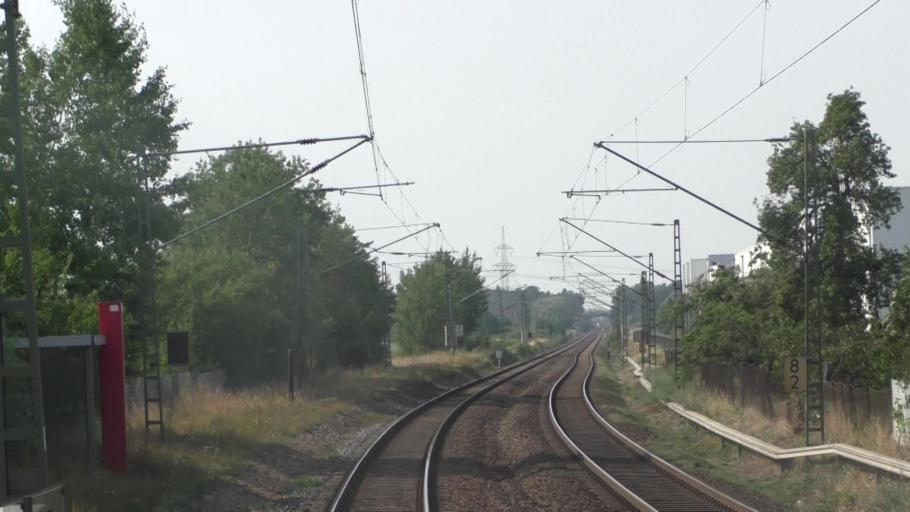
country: DE
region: Saxony-Anhalt
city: Zerbst
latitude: 51.9345
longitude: 12.1263
